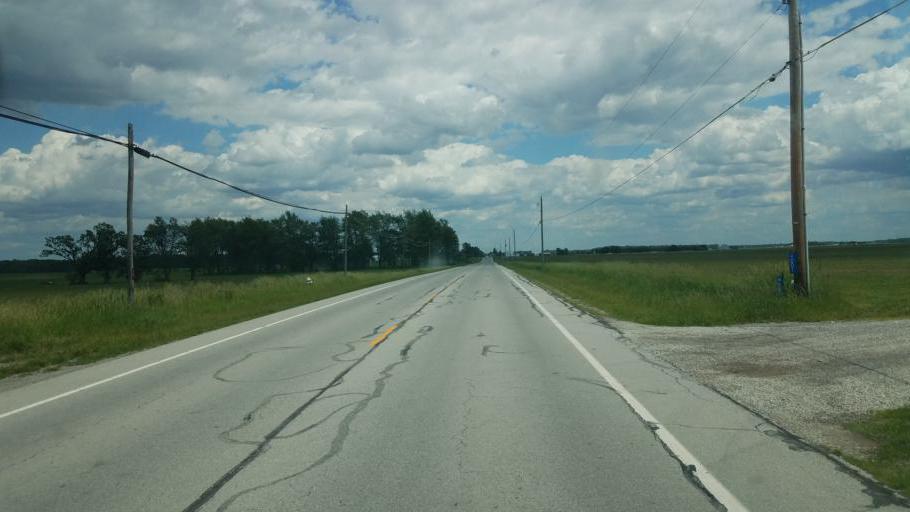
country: US
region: Ohio
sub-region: Crawford County
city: Bucyrus
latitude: 40.8127
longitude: -82.9211
